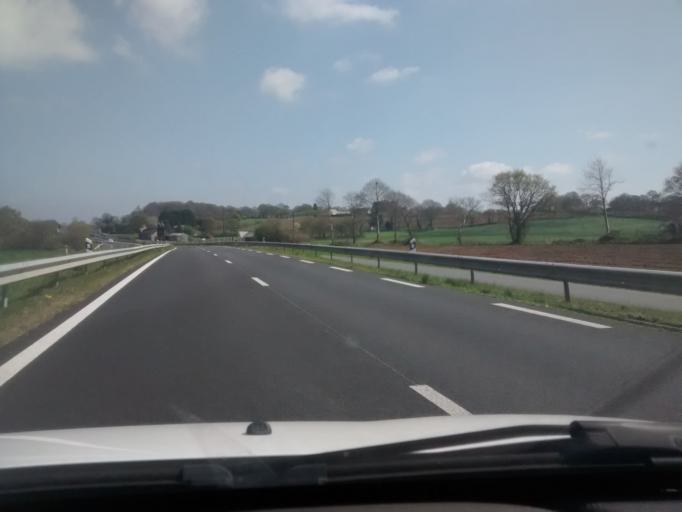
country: FR
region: Brittany
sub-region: Departement des Cotes-d'Armor
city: Pedernec
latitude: 48.5848
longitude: -3.2474
